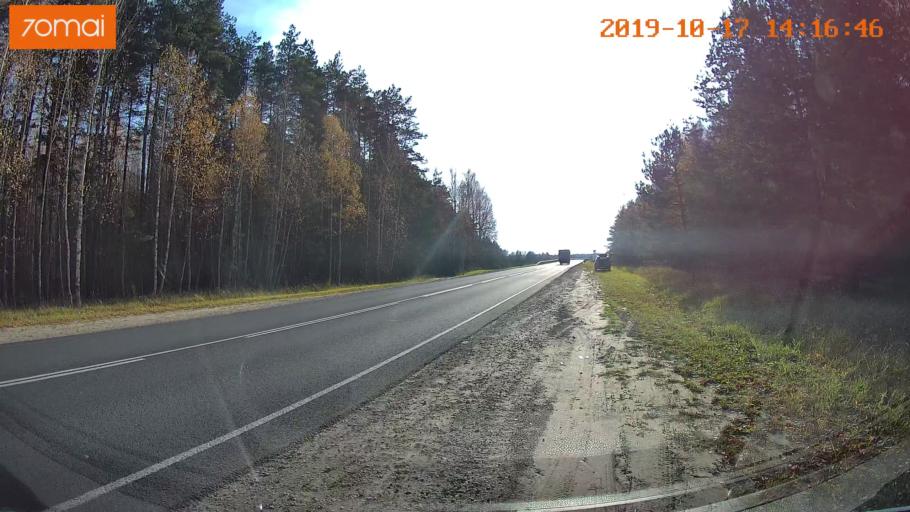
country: RU
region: Rjazan
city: Spas-Klepiki
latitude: 55.0782
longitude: 40.0496
